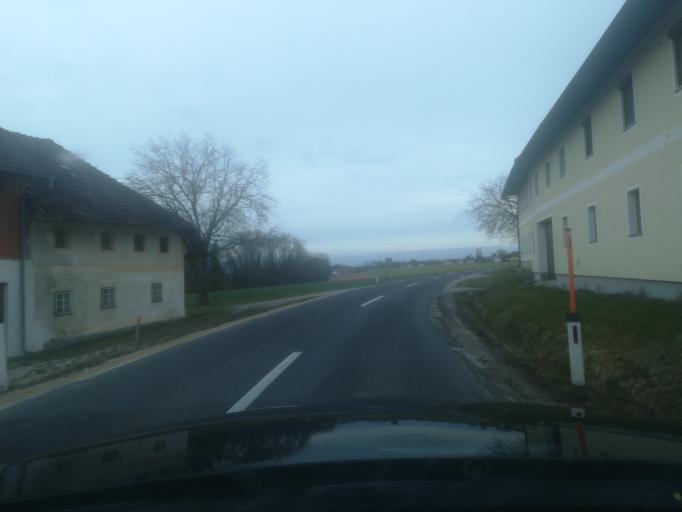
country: AT
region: Upper Austria
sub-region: Wels-Land
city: Gunskirchen
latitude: 48.1002
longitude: 13.9752
